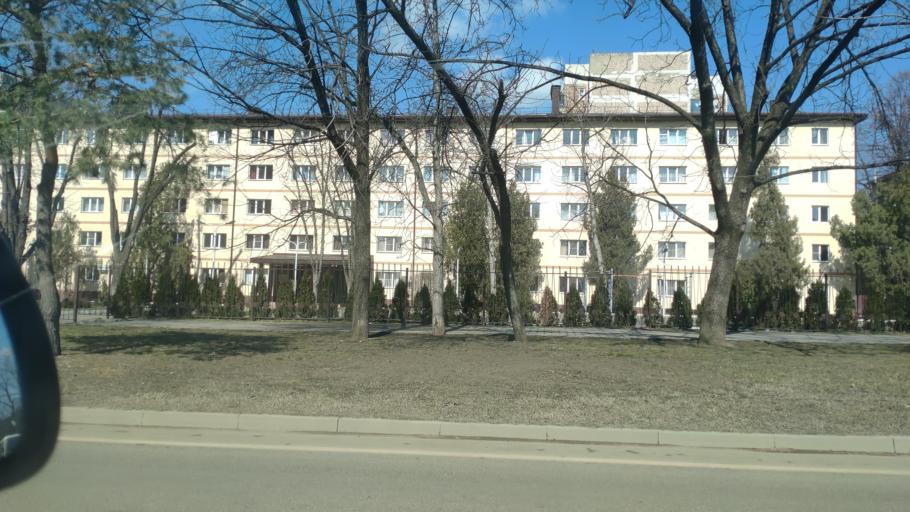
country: RU
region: Krasnodarskiy
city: Krasnodar
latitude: 45.0556
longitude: 39.0101
